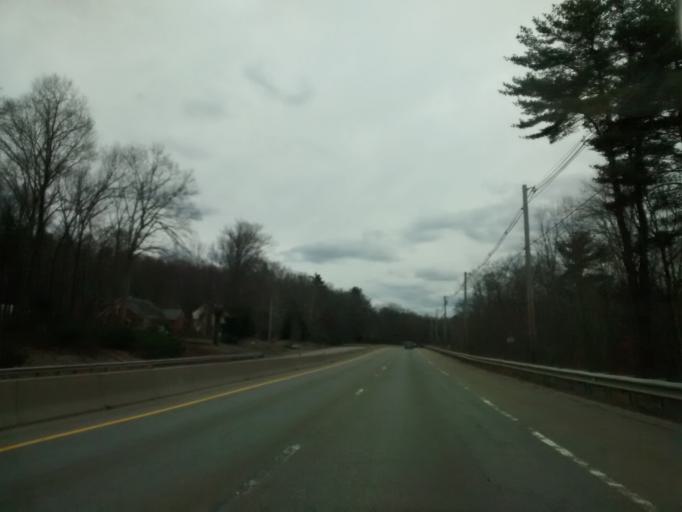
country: US
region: Massachusetts
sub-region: Worcester County
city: Charlton
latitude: 42.1481
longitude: -71.9317
